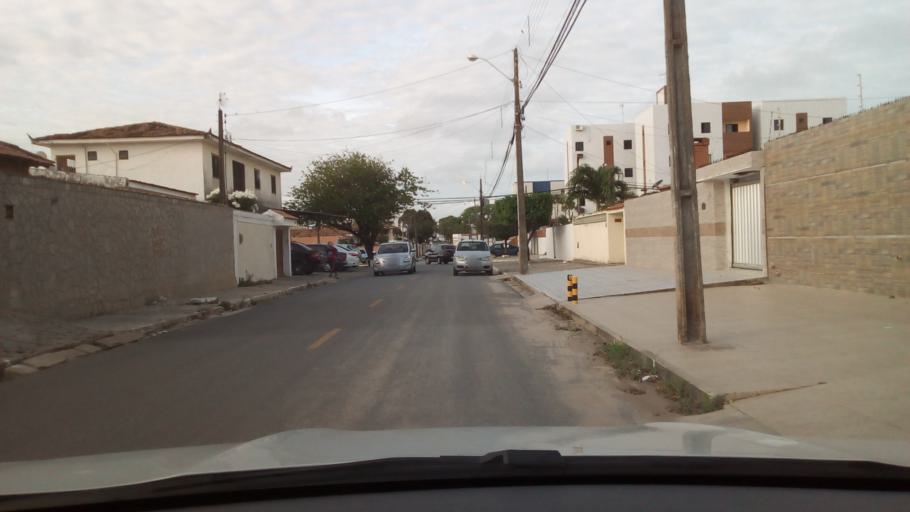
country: BR
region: Paraiba
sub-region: Joao Pessoa
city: Joao Pessoa
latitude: -7.1551
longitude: -34.8307
